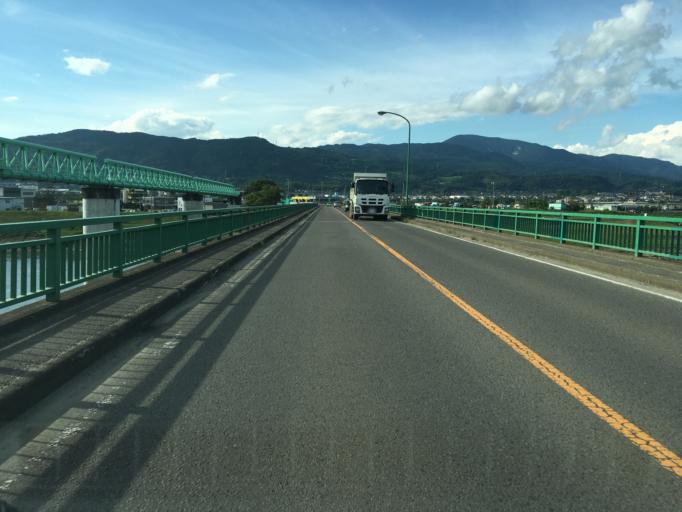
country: JP
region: Fukushima
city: Hobaramachi
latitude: 37.8287
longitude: 140.5198
